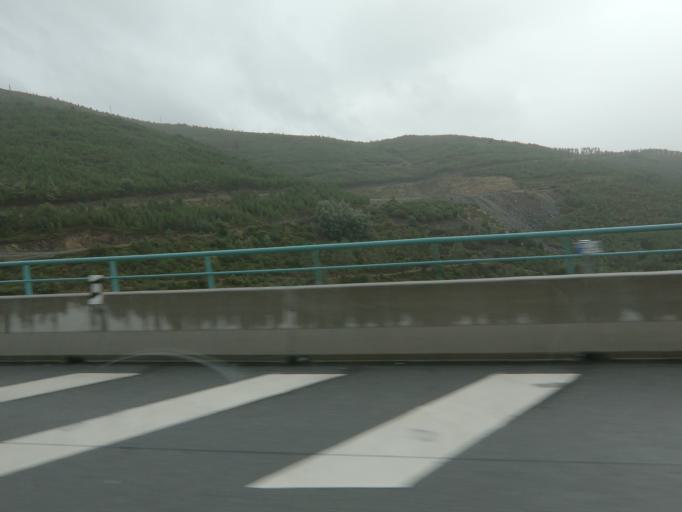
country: PT
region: Vila Real
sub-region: Mesao Frio
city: Mesao Frio
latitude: 41.2668
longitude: -7.9391
